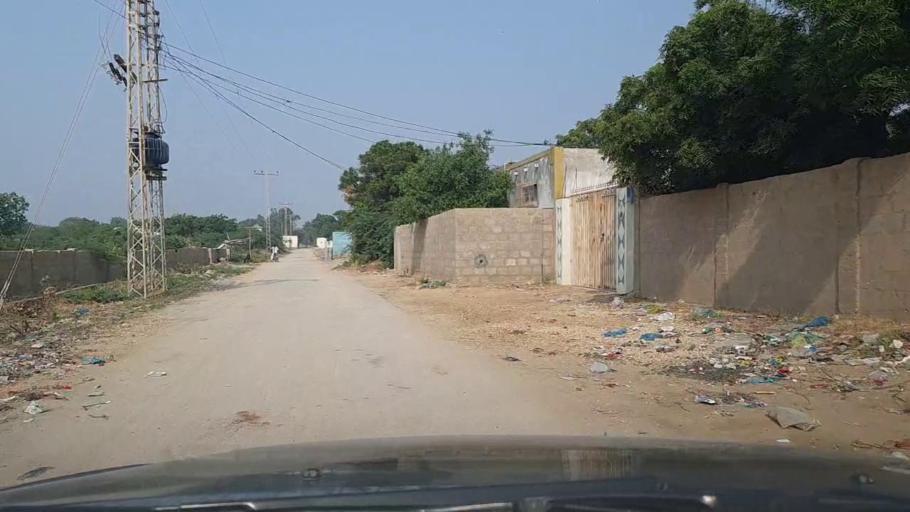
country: PK
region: Sindh
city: Thatta
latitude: 24.7435
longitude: 67.8957
